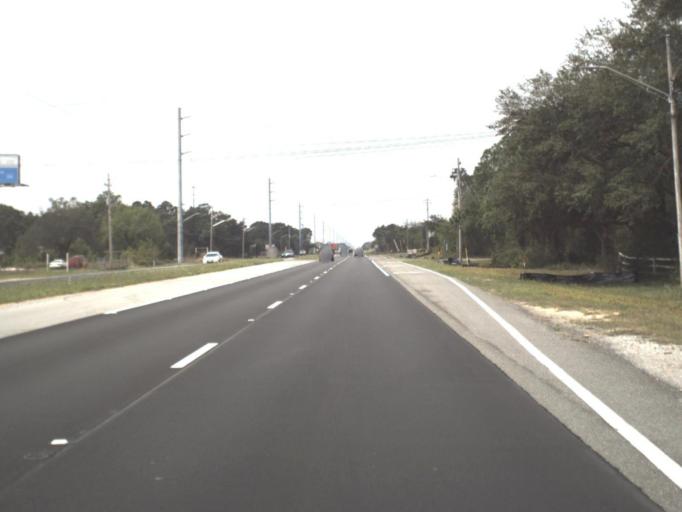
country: US
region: Florida
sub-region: Santa Rosa County
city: Tiger Point
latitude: 30.3954
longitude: -87.0299
